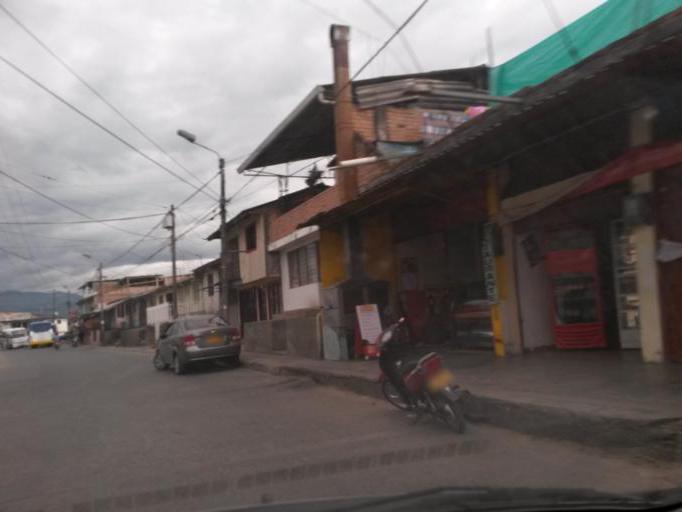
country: CO
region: Cauca
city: Popayan
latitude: 2.4480
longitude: -76.6302
